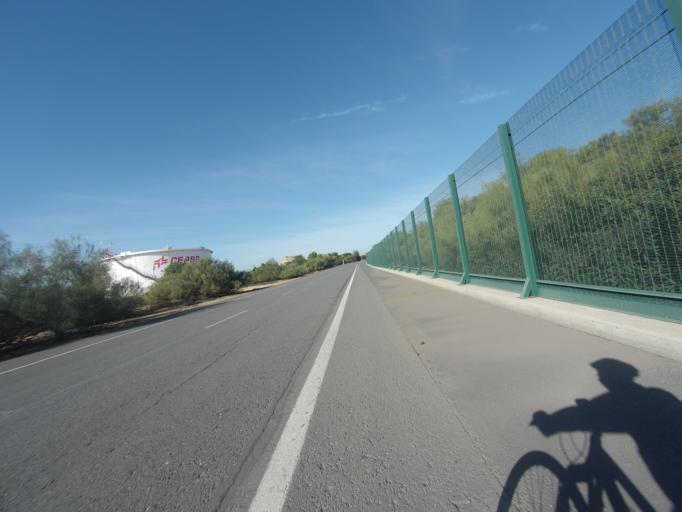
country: ES
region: Andalusia
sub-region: Provincia de Huelva
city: Punta Umbria
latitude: 37.2021
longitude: -6.9347
